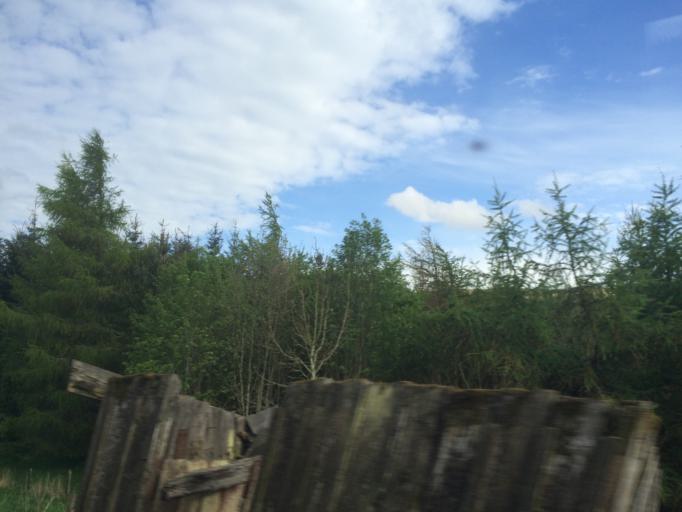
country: GB
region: Scotland
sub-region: Perth and Kinross
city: Auchterarder
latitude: 56.2613
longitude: -3.7480
